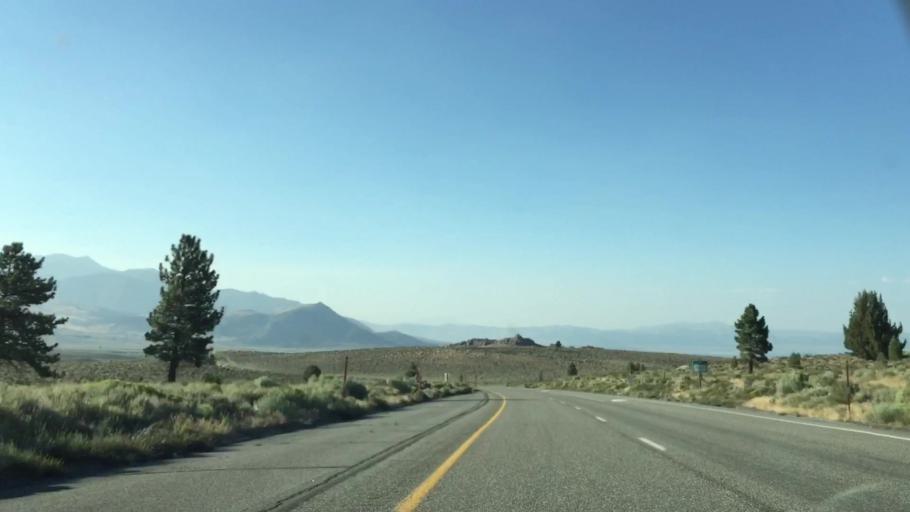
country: US
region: California
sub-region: Mono County
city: Mammoth Lakes
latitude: 37.8381
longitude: -119.0701
